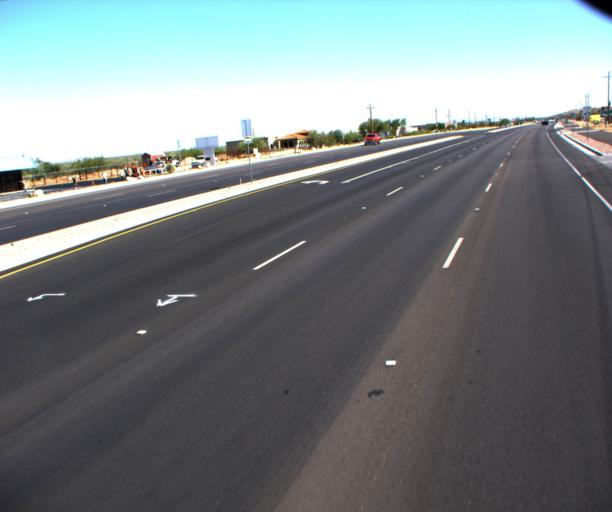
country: US
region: Arizona
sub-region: Pima County
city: Catalina
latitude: 32.4987
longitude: -110.9260
